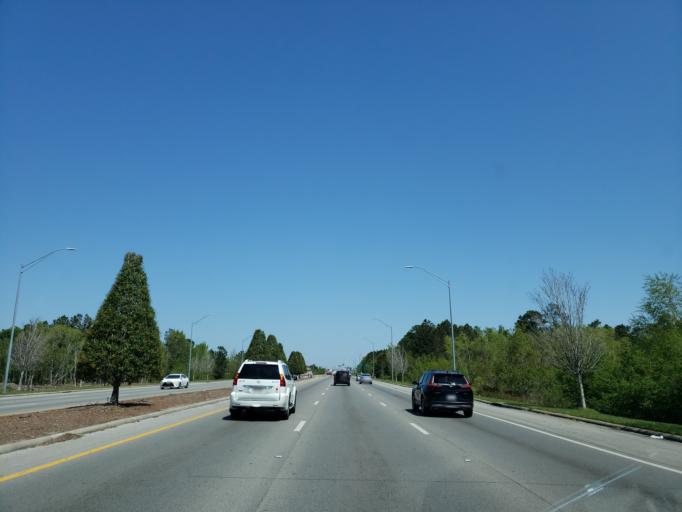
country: US
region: Mississippi
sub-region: Harrison County
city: West Gulfport
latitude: 30.4113
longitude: -89.0920
